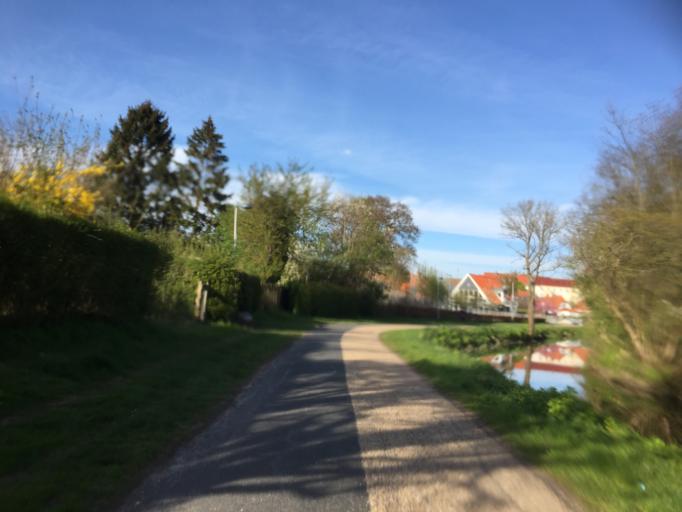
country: DK
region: Capital Region
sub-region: Gladsaxe Municipality
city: Buddinge
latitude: 55.7275
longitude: 12.5192
